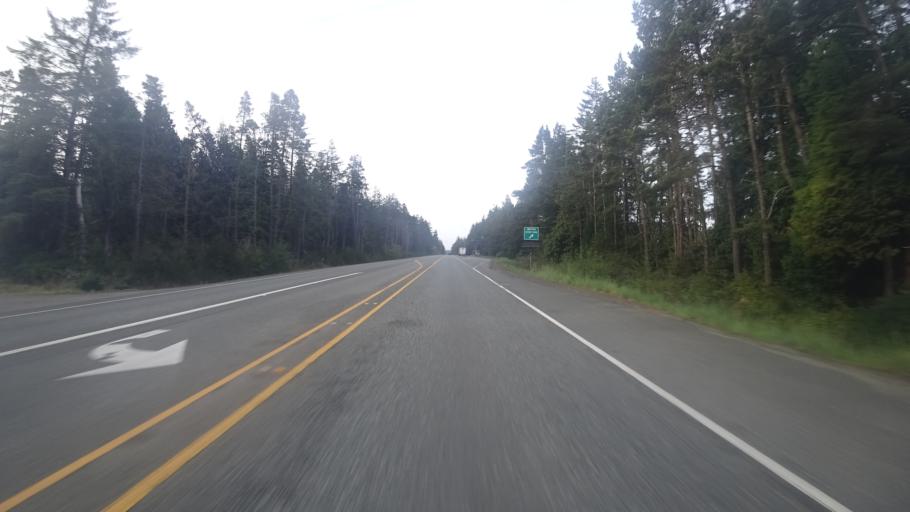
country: US
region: Oregon
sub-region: Coos County
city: Lakeside
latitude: 43.5147
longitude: -124.2172
